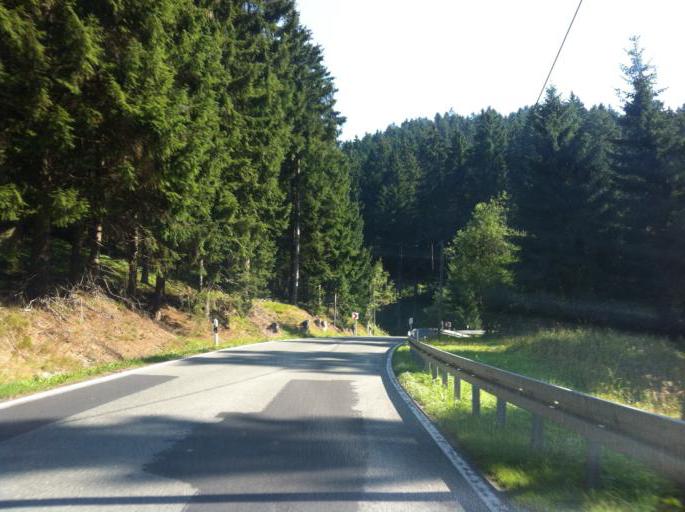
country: DE
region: Thuringia
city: Steinheid
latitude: 50.4662
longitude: 11.0685
